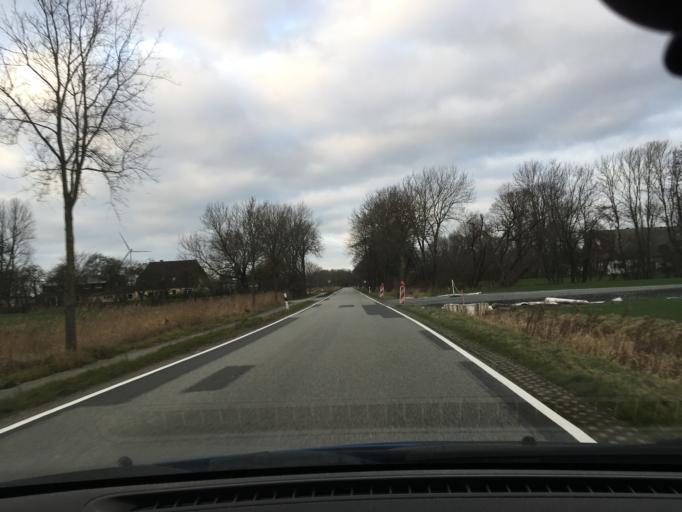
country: DE
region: Schleswig-Holstein
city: Norderwohrden
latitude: 54.1938
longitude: 9.0356
